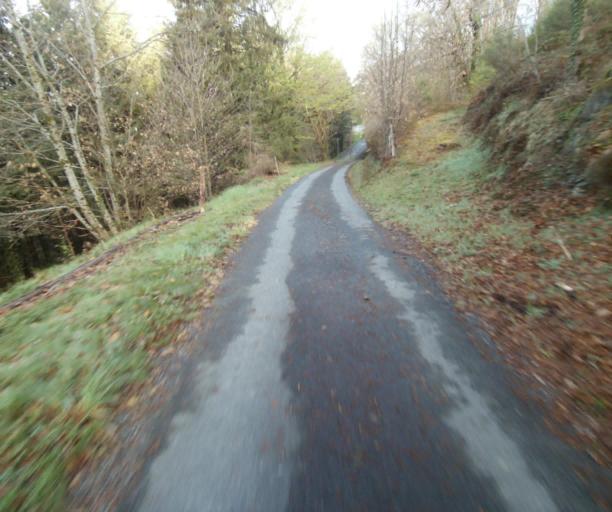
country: FR
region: Limousin
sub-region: Departement de la Correze
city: Naves
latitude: 45.3029
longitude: 1.8421
